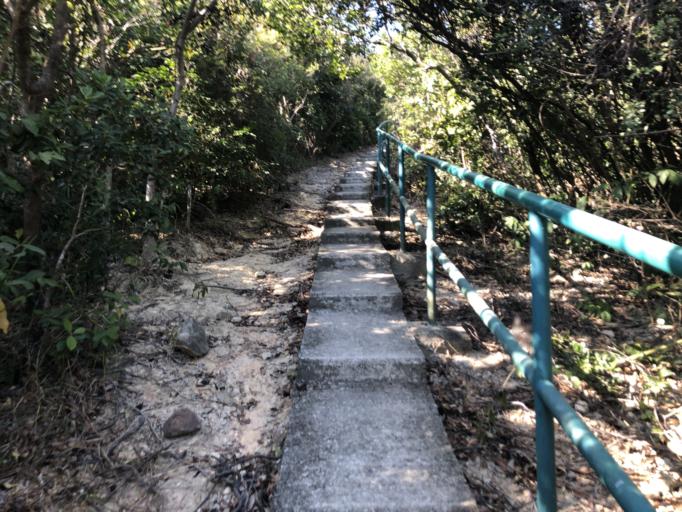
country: HK
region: Wanchai
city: Wan Chai
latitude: 22.2224
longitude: 114.2045
